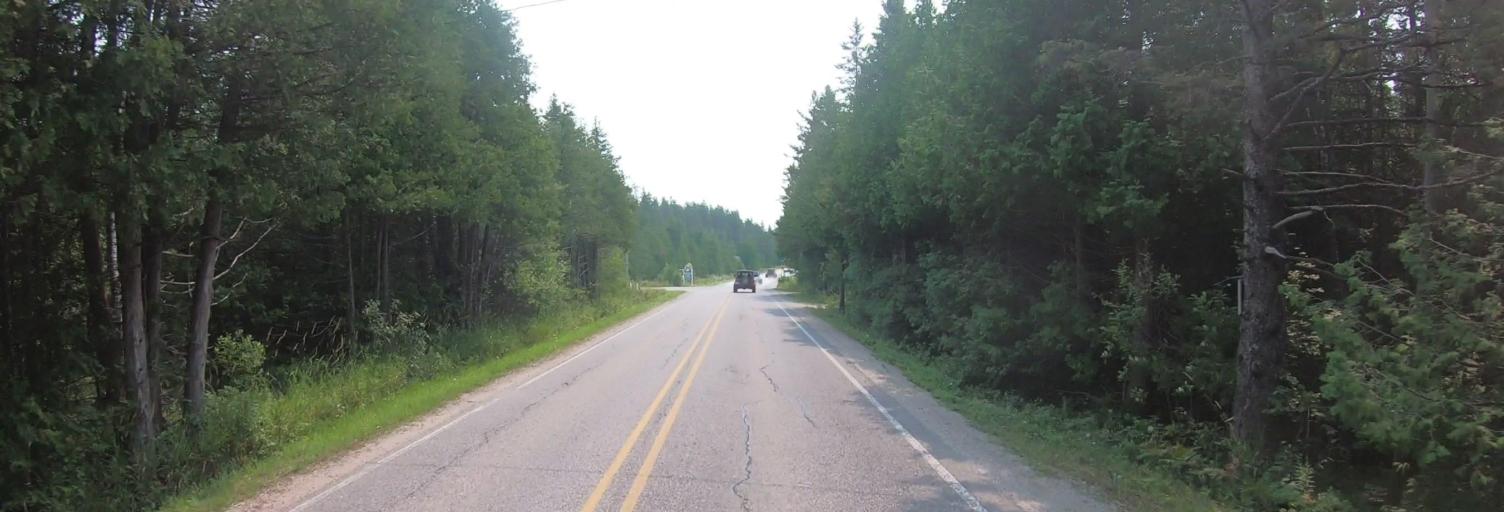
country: CA
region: Ontario
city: Thessalon
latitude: 45.9914
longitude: -83.6990
